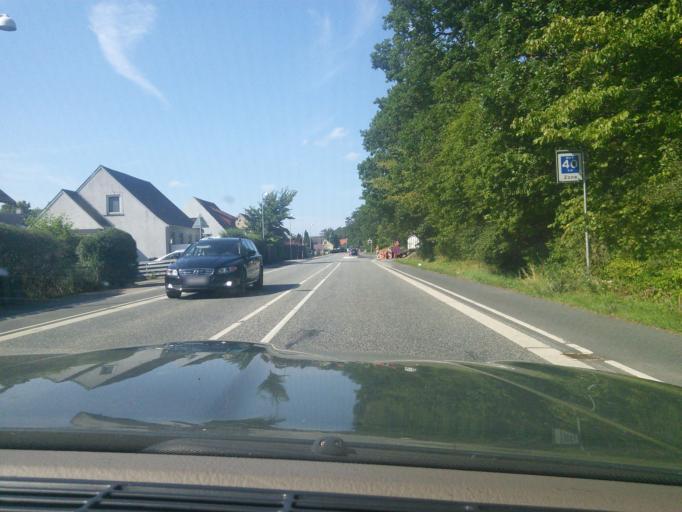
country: DK
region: Capital Region
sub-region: Halsnaes Kommune
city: Frederiksvaerk
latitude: 55.9835
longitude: 12.0197
